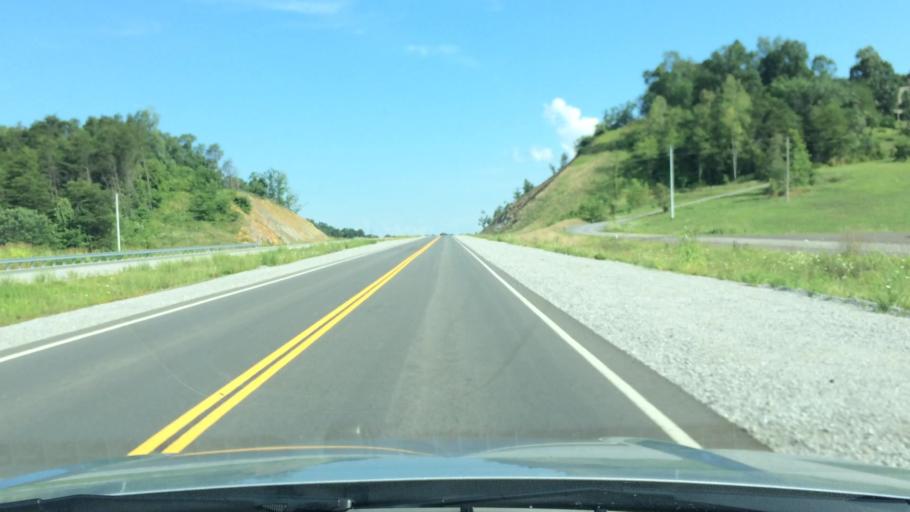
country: US
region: Tennessee
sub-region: Jefferson County
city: White Pine
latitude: 36.1345
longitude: -83.3366
